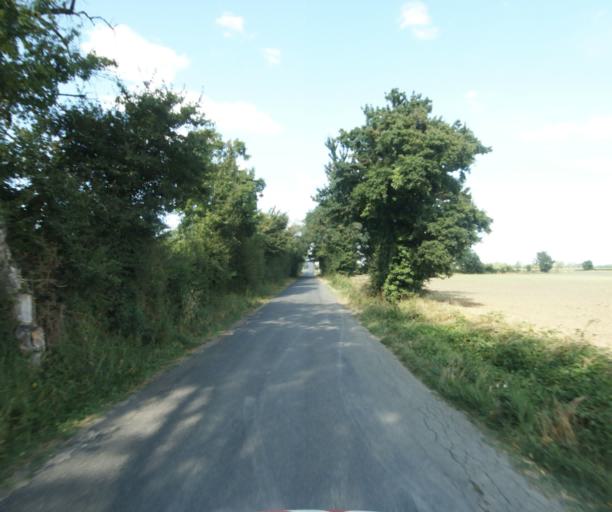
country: FR
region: Midi-Pyrenees
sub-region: Departement du Tarn
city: Puylaurens
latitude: 43.5185
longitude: 1.9621
